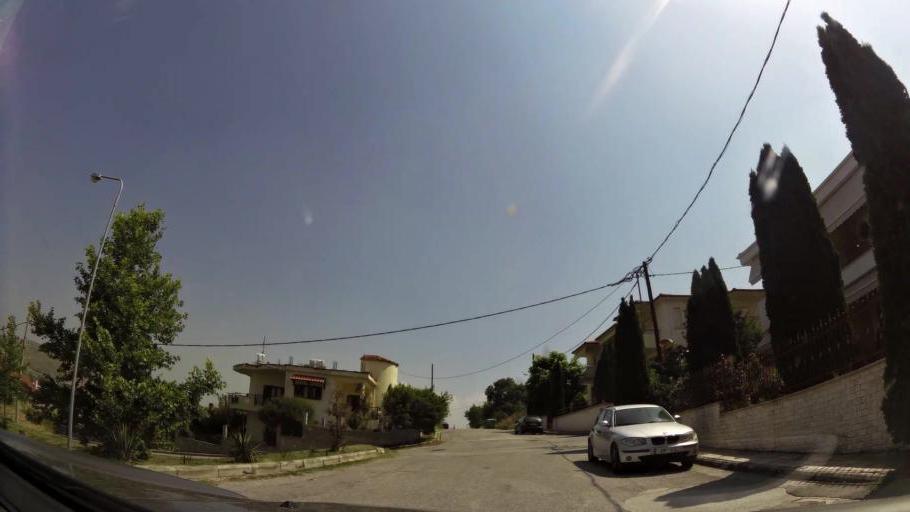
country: GR
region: West Macedonia
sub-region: Nomos Kozanis
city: Koila
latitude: 40.3264
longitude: 21.7932
